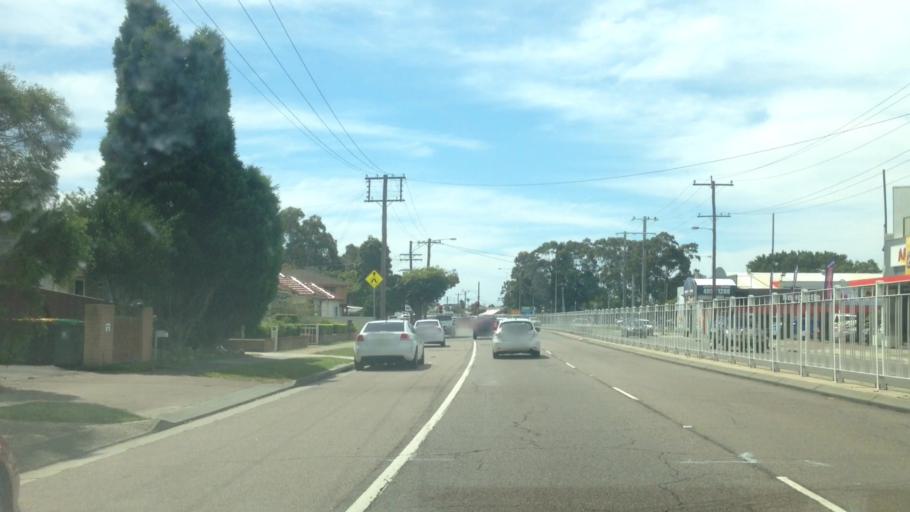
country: AU
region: New South Wales
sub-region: Newcastle
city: Broadmeadow
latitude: -32.9169
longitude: 151.7251
